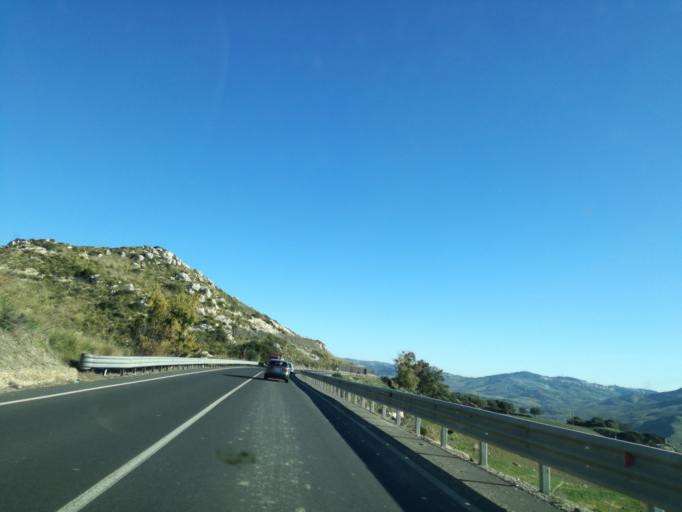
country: IT
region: Sicily
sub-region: Catania
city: San Michele di Ganzaria
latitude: 37.2162
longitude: 14.4218
